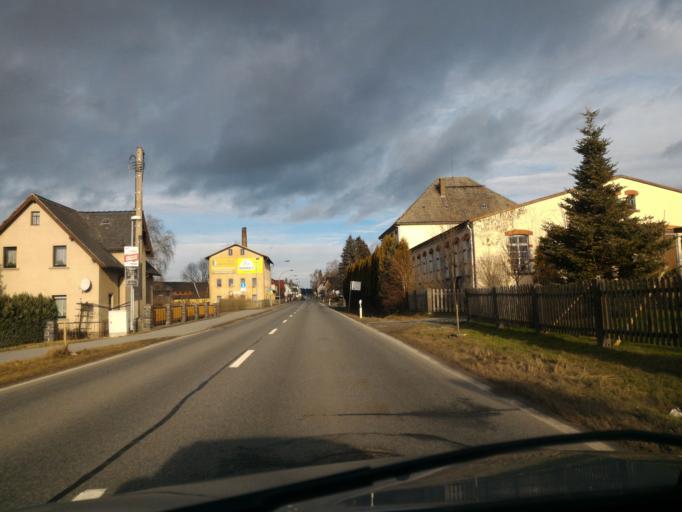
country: DE
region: Saxony
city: Oppach
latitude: 51.0489
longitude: 14.5104
